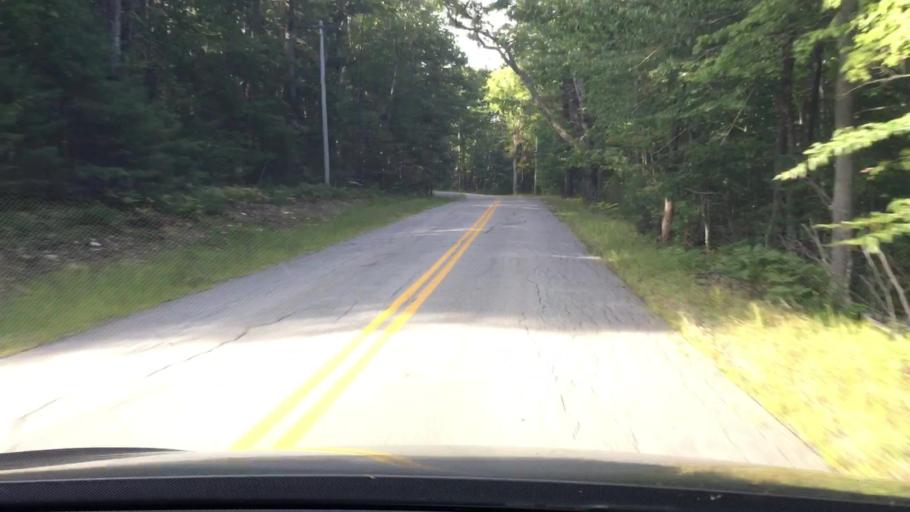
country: US
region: Maine
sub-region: Hancock County
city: Orland
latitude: 44.5294
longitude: -68.7635
